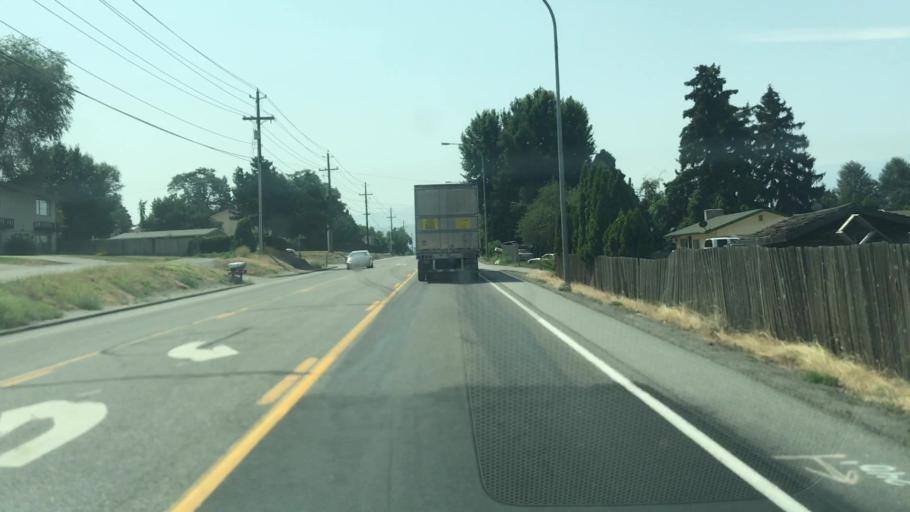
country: US
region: Washington
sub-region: Douglas County
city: East Wenatchee Bench
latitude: 47.4590
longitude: -120.2974
